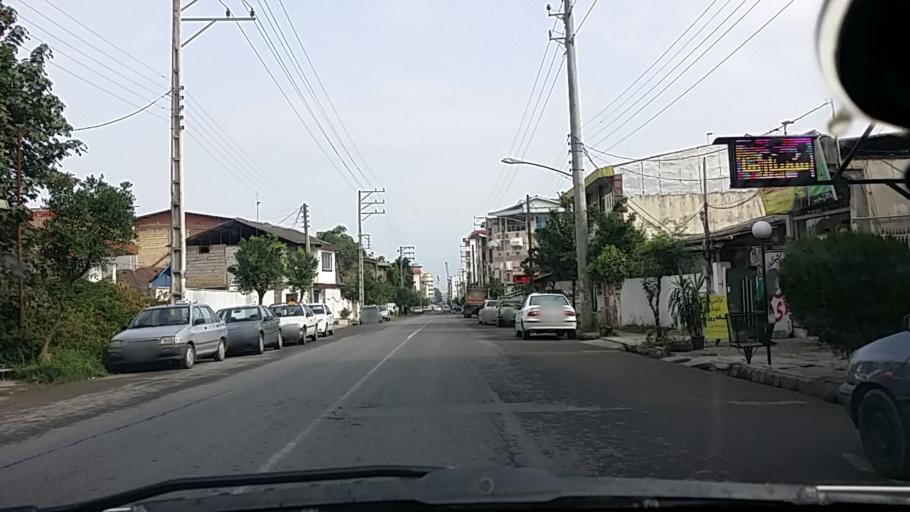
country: IR
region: Mazandaran
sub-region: Nowshahr
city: Nowshahr
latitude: 36.6431
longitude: 51.5083
